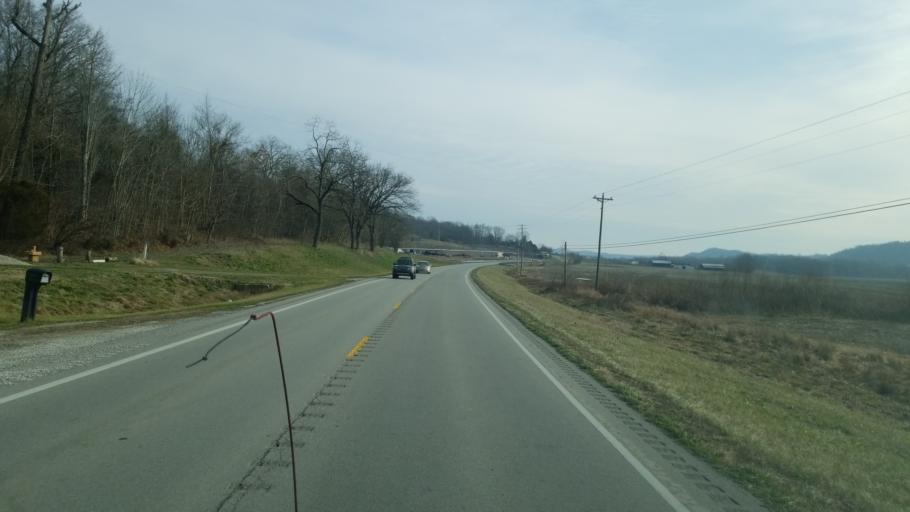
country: US
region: Kentucky
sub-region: Casey County
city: Liberty
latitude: 37.3446
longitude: -84.8922
